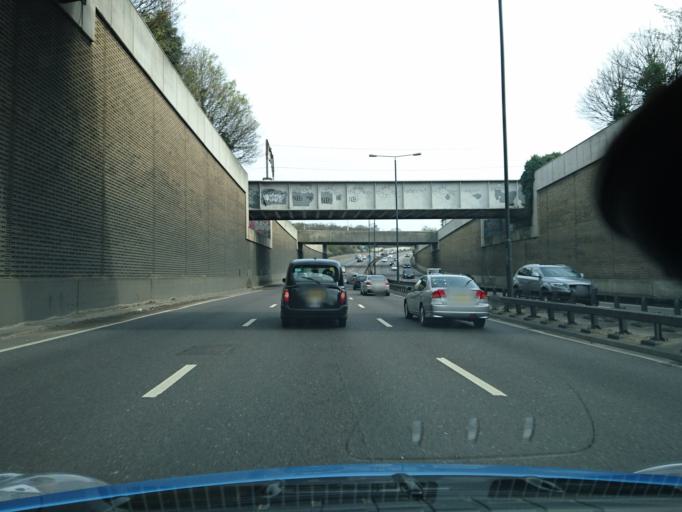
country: GB
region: England
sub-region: Greater London
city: Walthamstow
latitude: 51.6005
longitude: -0.0042
